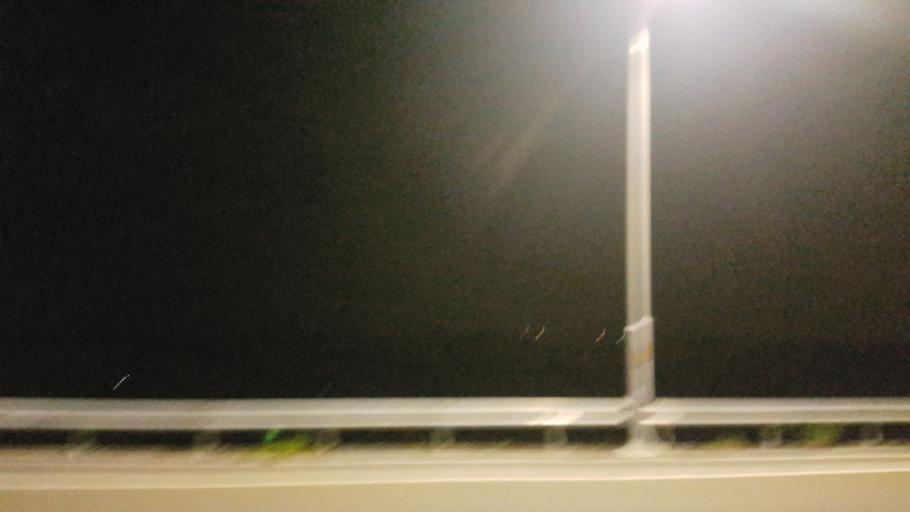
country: TW
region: Taiwan
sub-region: Hsinchu
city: Hsinchu
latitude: 24.7481
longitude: 120.9609
